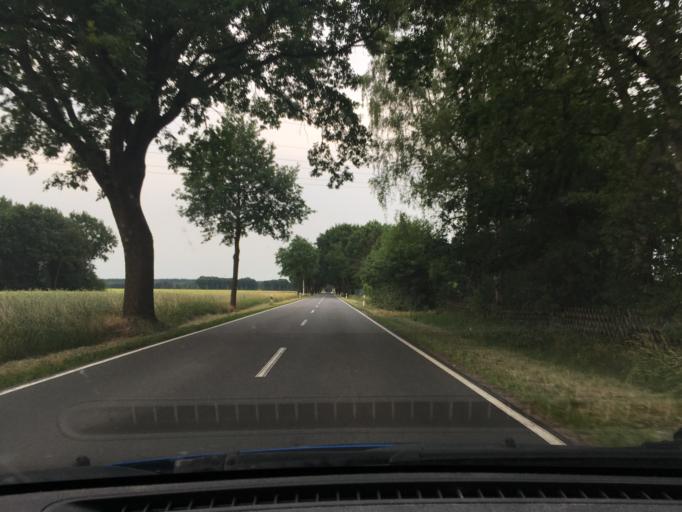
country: DE
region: Lower Saxony
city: Walsrode
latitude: 52.8362
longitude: 9.6406
